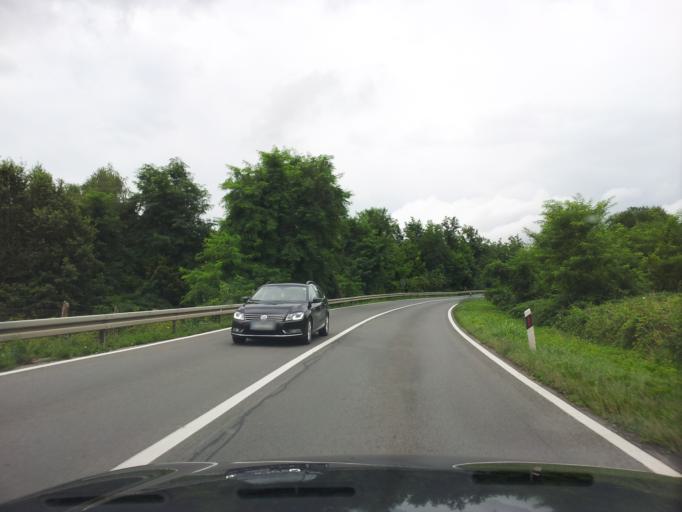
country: HR
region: Karlovacka
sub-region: Grad Karlovac
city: Karlovac
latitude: 45.4422
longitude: 15.5863
